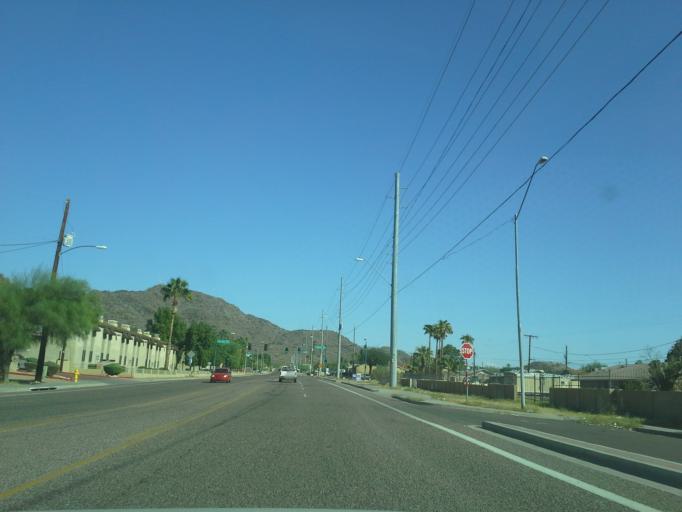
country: US
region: Arizona
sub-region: Maricopa County
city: Glendale
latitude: 33.5820
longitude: -112.0929
